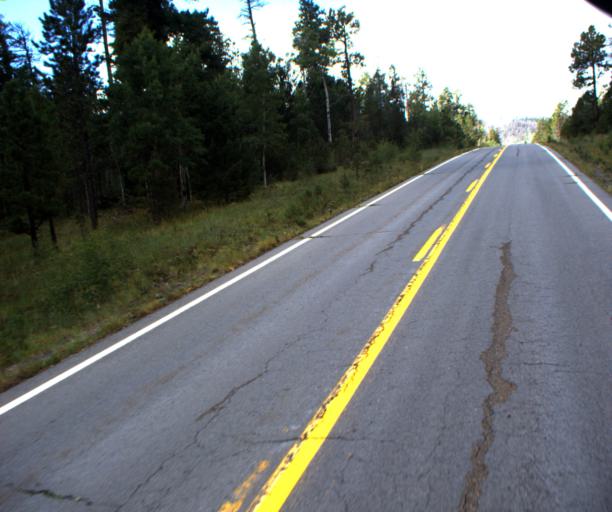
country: US
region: Arizona
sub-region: Apache County
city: Eagar
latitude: 34.0092
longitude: -109.3657
